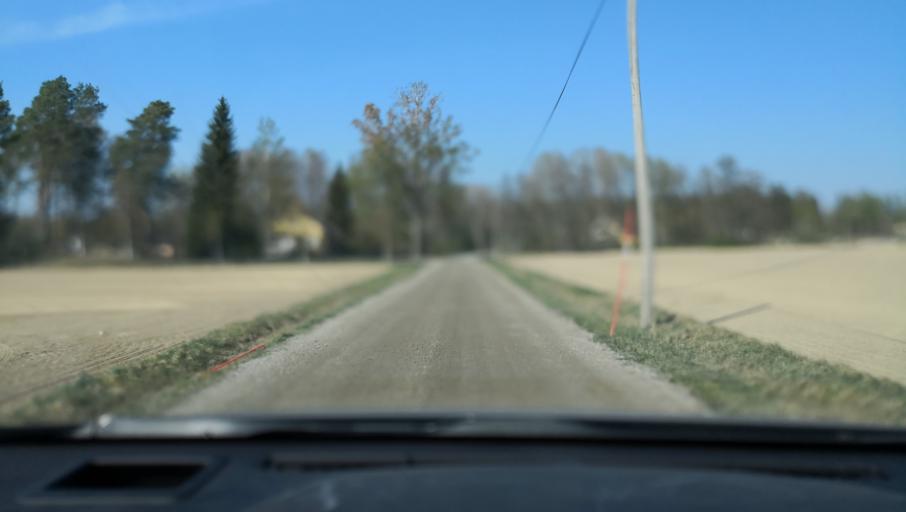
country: SE
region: Uppsala
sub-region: Heby Kommun
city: Heby
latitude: 60.0333
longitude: 16.7825
